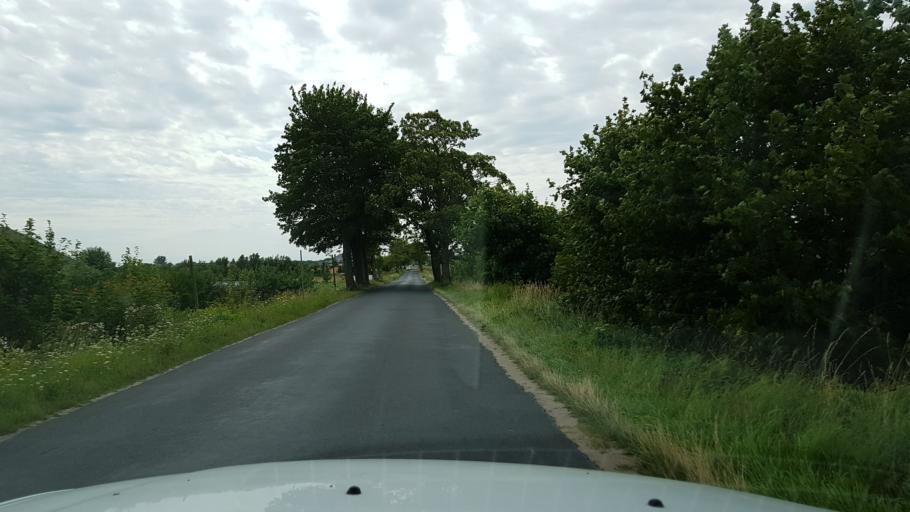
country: PL
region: West Pomeranian Voivodeship
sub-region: Powiat koszalinski
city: Mielno
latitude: 54.2377
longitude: 15.9733
